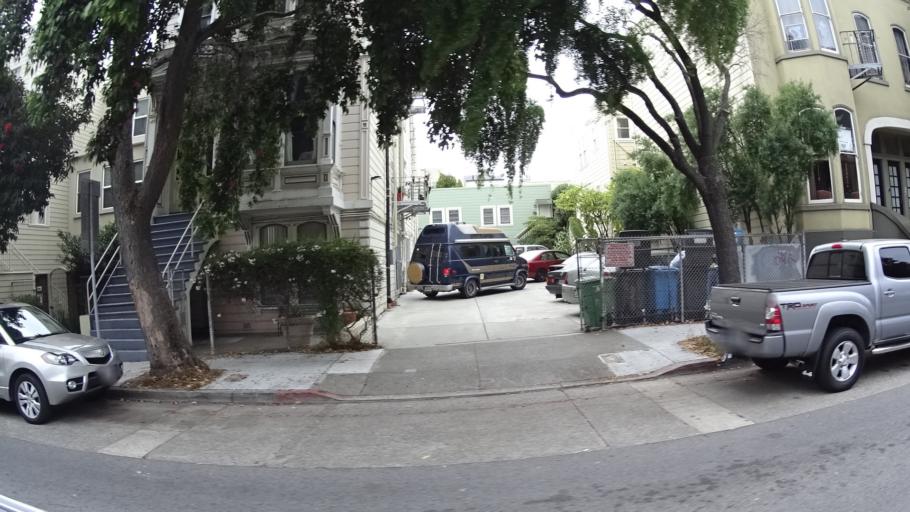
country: US
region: California
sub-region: San Francisco County
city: San Francisco
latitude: 37.7874
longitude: -122.4380
